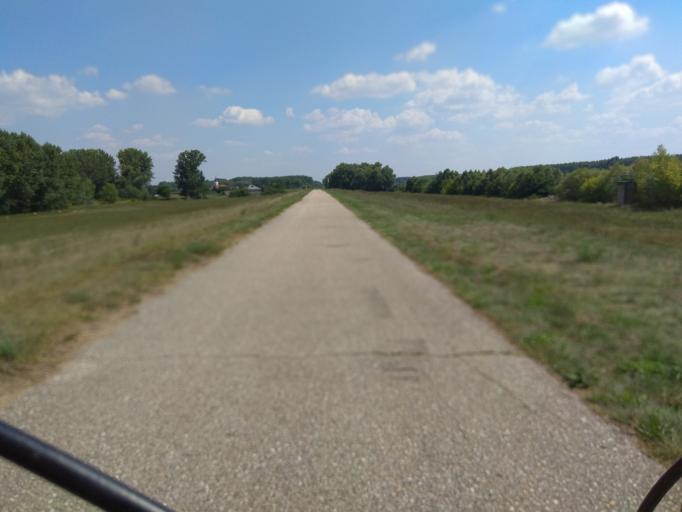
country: SK
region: Trnavsky
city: Gabcikovo
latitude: 47.8244
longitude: 17.6086
